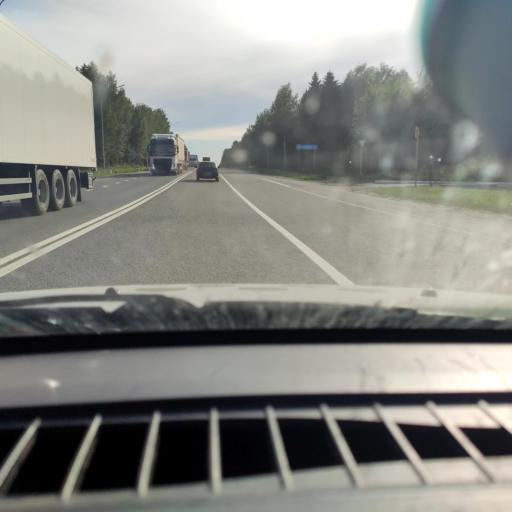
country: RU
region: Kirov
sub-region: Kirovo-Chepetskiy Rayon
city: Kirov
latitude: 58.6379
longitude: 49.8400
